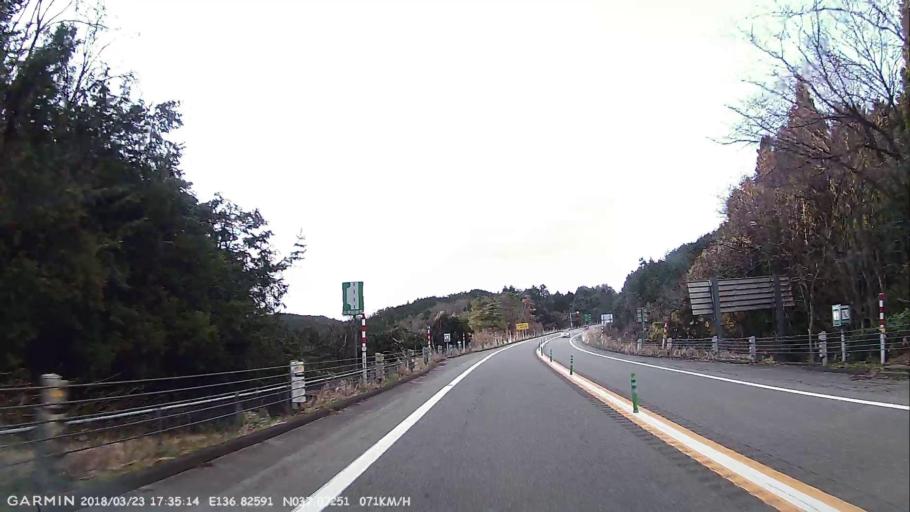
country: JP
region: Ishikawa
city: Nanao
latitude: 37.0727
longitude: 136.8258
